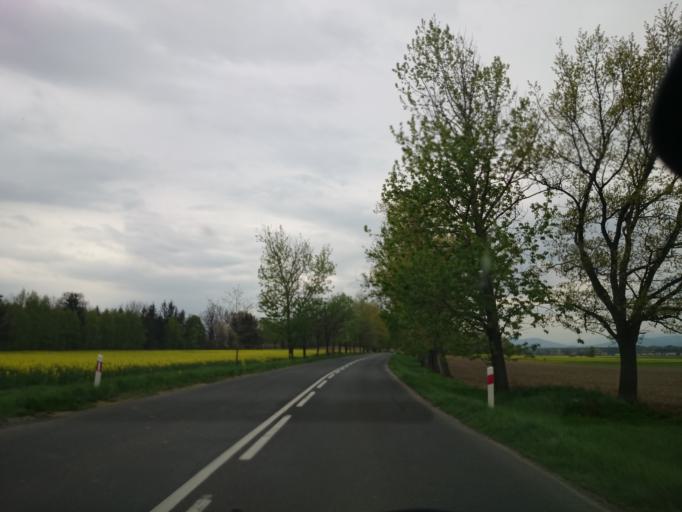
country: PL
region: Opole Voivodeship
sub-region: Powiat nyski
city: Nysa
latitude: 50.4293
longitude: 17.3412
